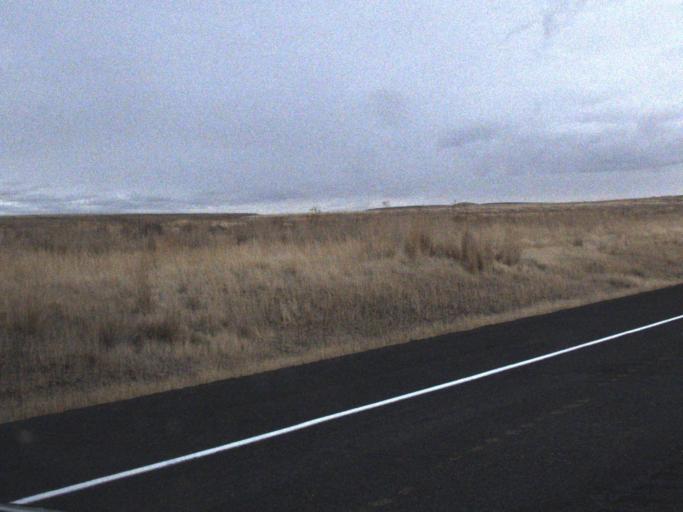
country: US
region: Washington
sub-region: Adams County
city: Ritzville
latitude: 46.7485
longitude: -118.2577
